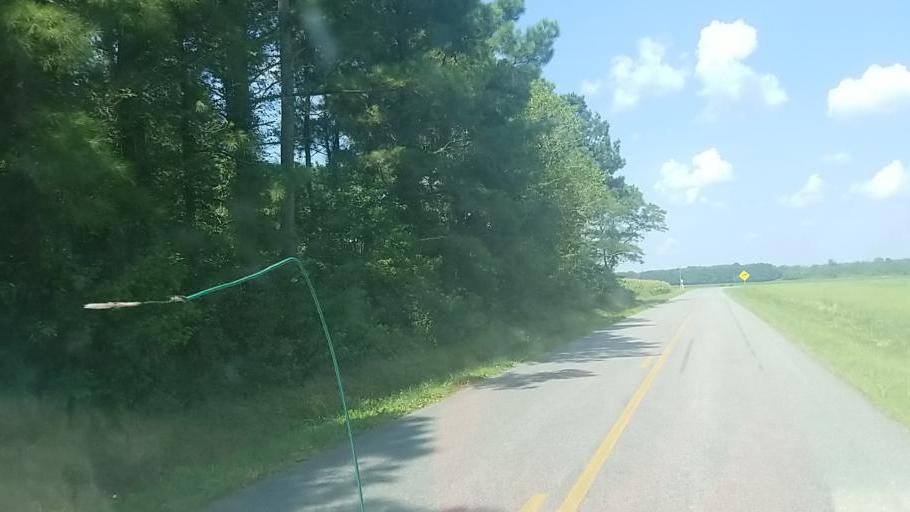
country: US
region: Maryland
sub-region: Worcester County
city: Berlin
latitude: 38.2976
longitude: -75.2688
